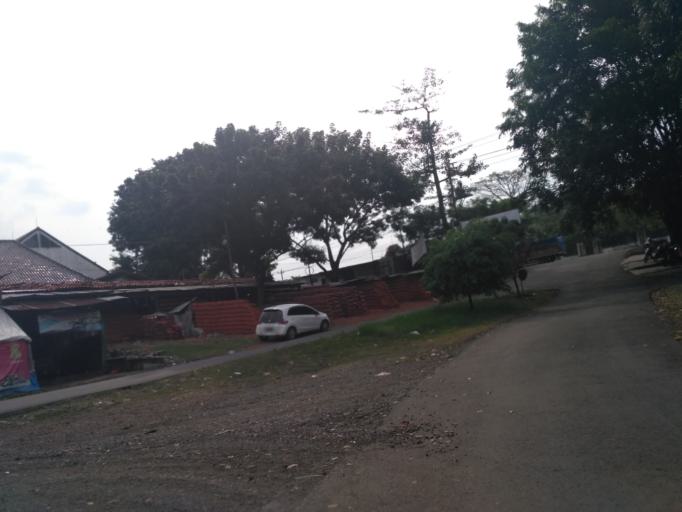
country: ID
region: Central Java
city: Semarang
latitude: -6.9879
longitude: 110.3720
